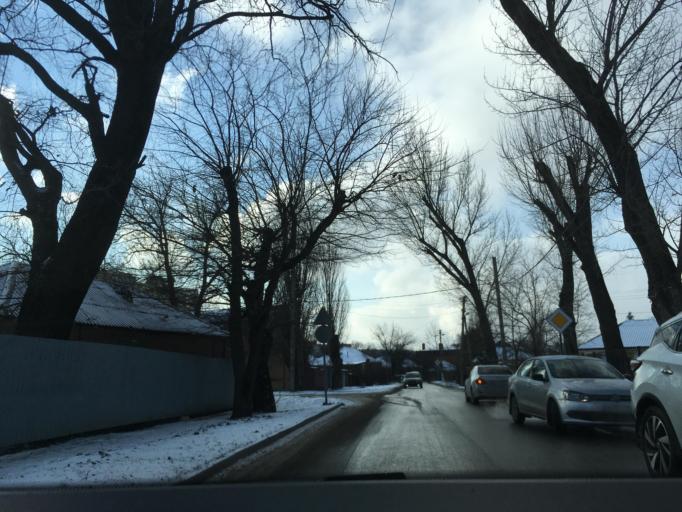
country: RU
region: Rostov
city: Rostov-na-Donu
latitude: 47.2347
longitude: 39.6340
